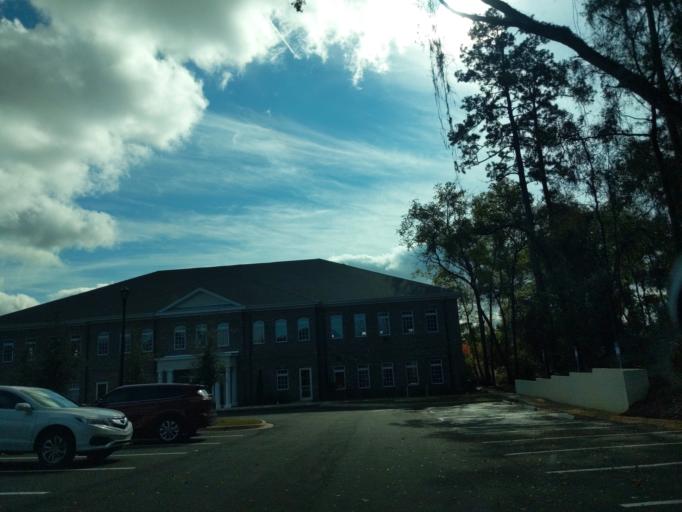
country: US
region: Florida
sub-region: Leon County
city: Tallahassee
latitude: 30.4678
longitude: -84.2093
